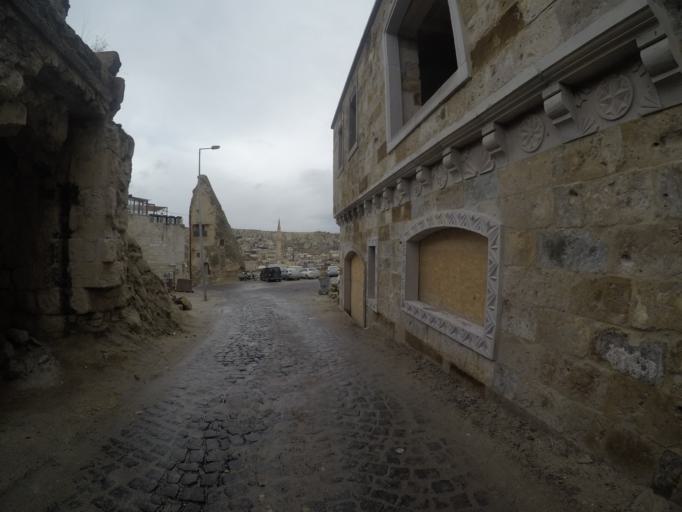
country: TR
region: Nevsehir
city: Goereme
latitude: 38.6411
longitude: 34.8310
